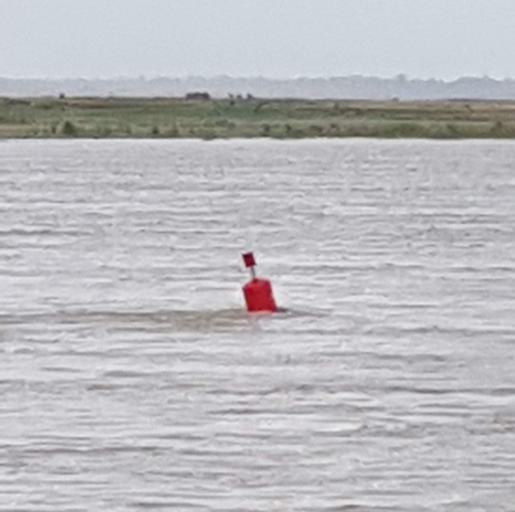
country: MM
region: Magway
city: Pakokku
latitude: 21.2639
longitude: 94.9864
